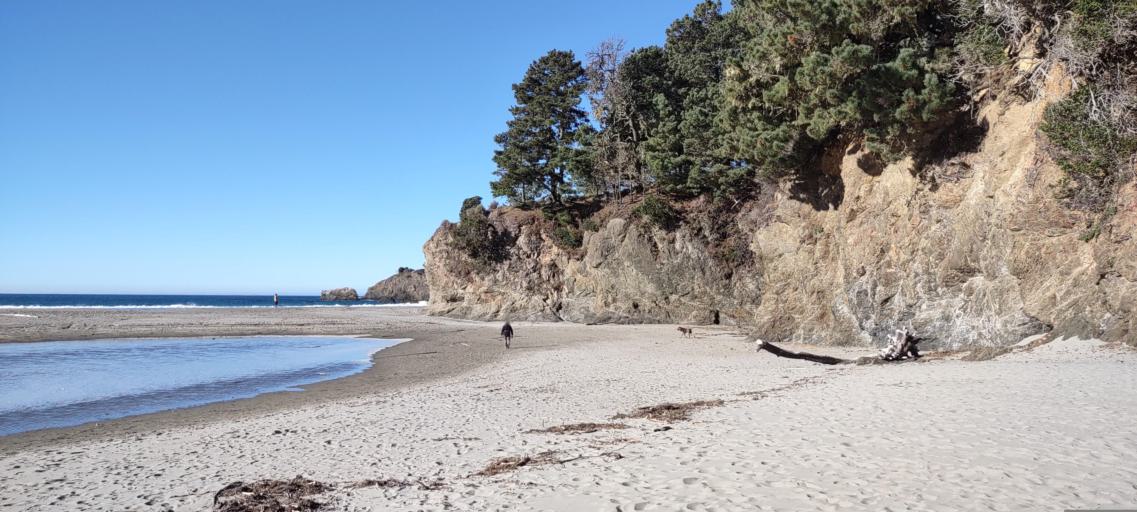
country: US
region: California
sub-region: Mendocino County
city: Fort Bragg
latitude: 39.3033
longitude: -123.7957
